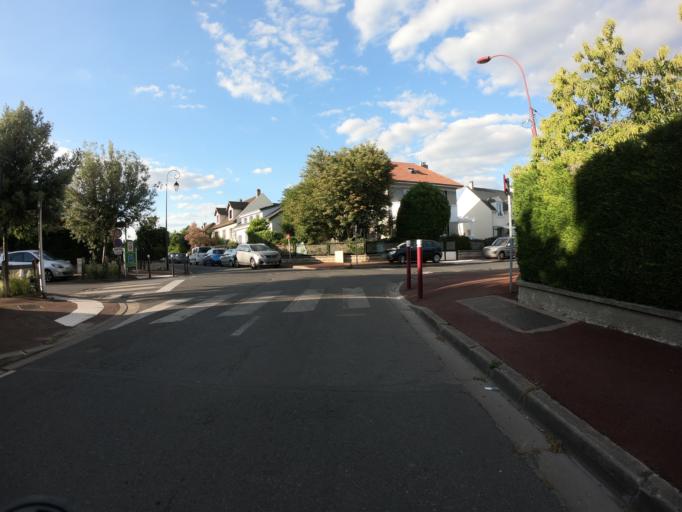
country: FR
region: Ile-de-France
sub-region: Departement du Val-de-Marne
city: Fresnes
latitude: 48.7601
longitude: 2.3133
